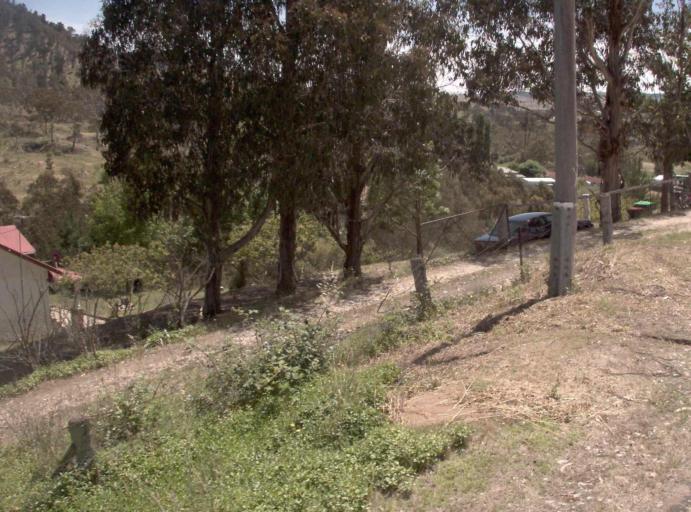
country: AU
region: Victoria
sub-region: Alpine
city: Mount Beauty
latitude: -37.1023
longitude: 147.5882
